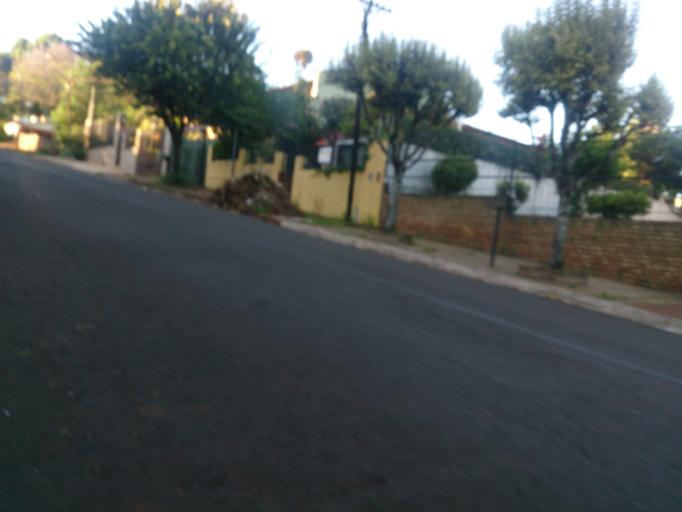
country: AR
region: Misiones
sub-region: Departamento de Obera
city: Obera
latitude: -27.4913
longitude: -55.1248
